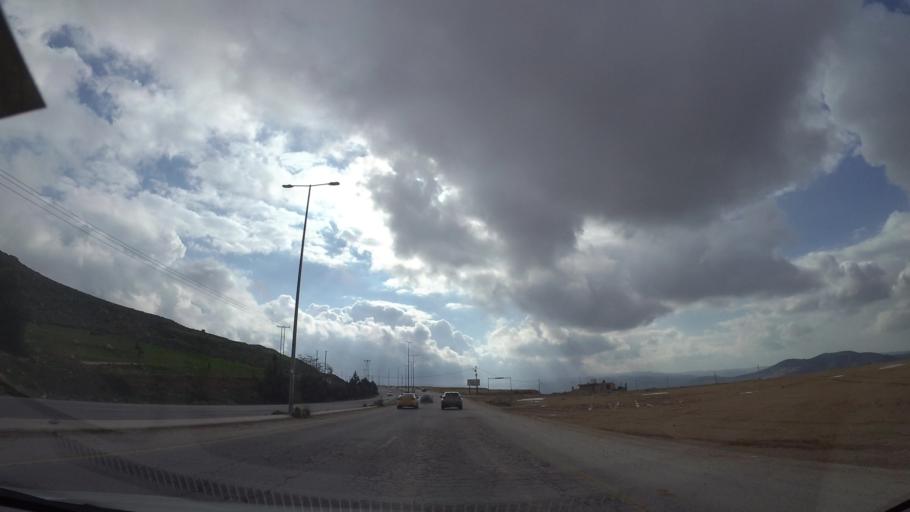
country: JO
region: Amman
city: Al Jubayhah
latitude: 32.0831
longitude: 35.8828
